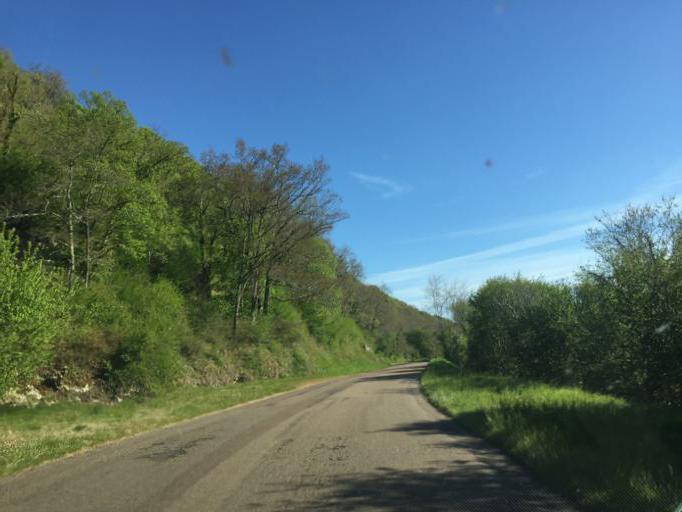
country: FR
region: Bourgogne
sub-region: Departement de la Nievre
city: Clamecy
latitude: 47.4934
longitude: 3.5073
